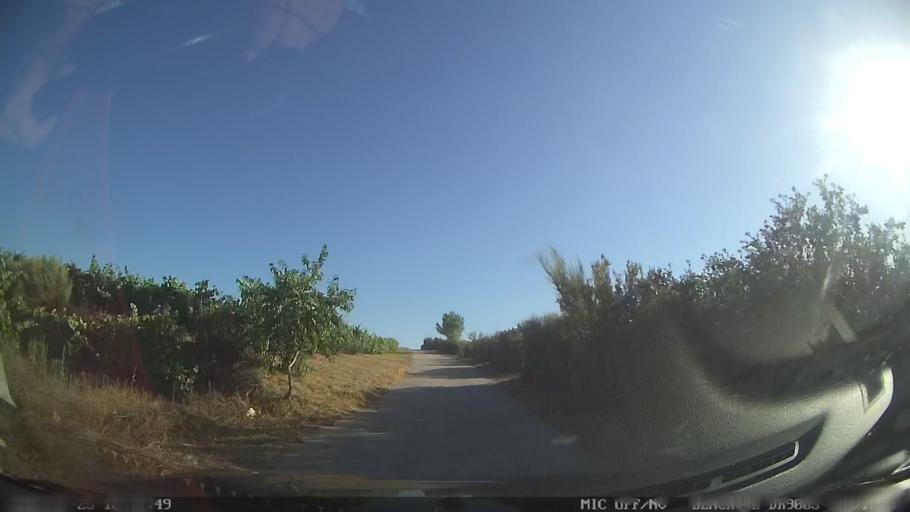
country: PT
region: Viseu
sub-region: Sao Joao da Pesqueira
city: Sao Joao da Pesqueira
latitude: 41.1625
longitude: -7.4154
